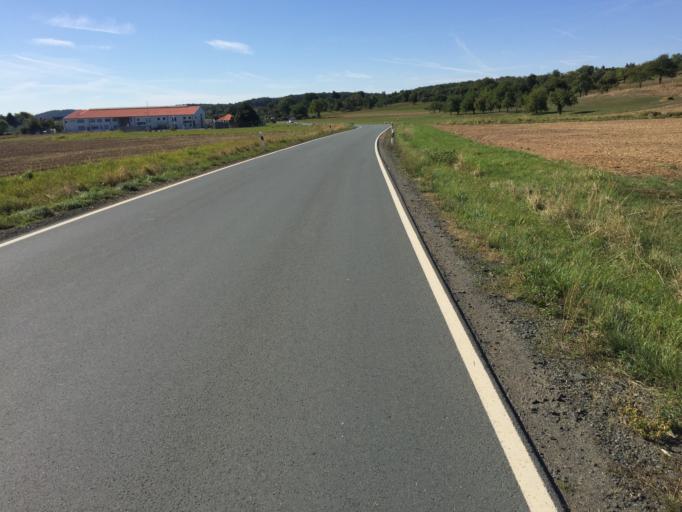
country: DE
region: Hesse
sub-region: Regierungsbezirk Giessen
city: Reiskirchen
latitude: 50.5996
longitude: 8.8422
